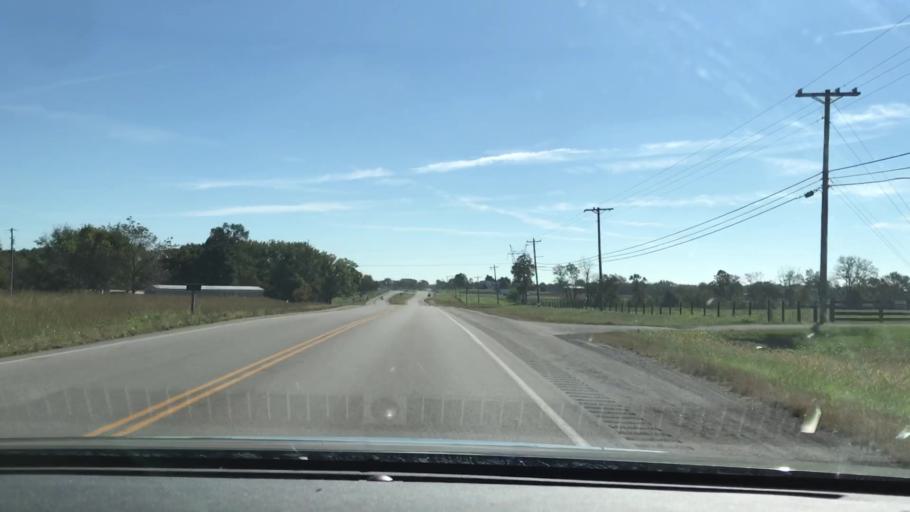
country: US
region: Kentucky
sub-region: Christian County
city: Hopkinsville
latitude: 36.8595
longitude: -87.4312
